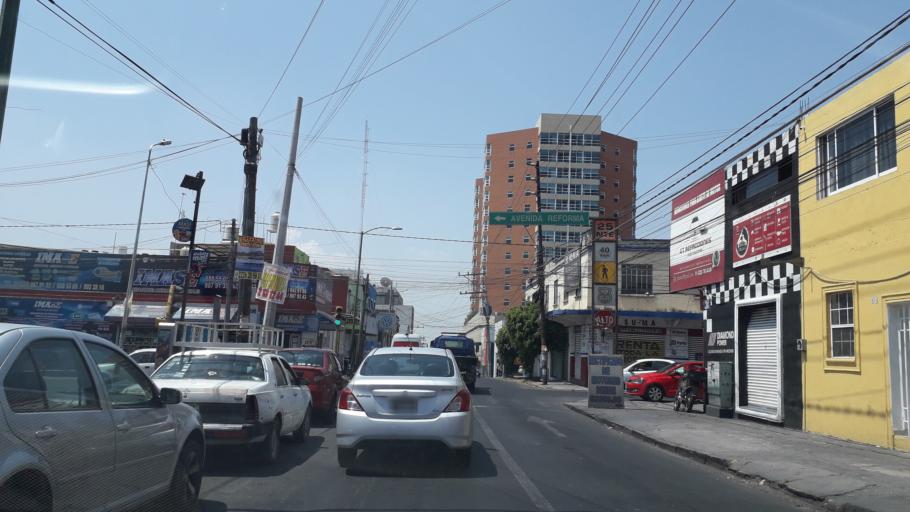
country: MX
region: Puebla
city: Puebla
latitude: 19.0538
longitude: -98.2165
